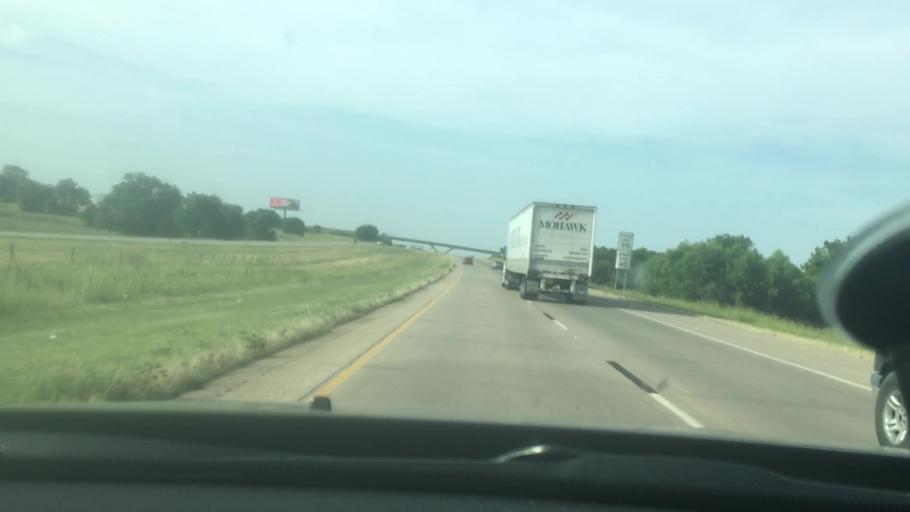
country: US
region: Oklahoma
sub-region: Carter County
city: Ardmore
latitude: 34.3238
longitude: -97.1556
